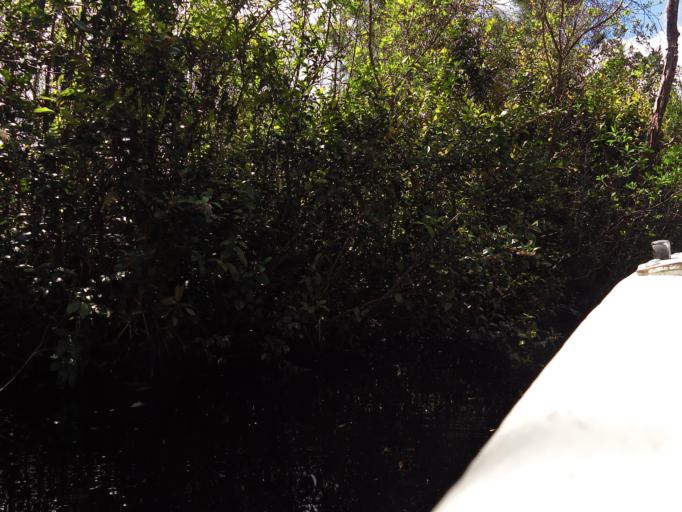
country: US
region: Georgia
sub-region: Charlton County
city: Folkston
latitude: 30.7376
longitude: -82.1424
